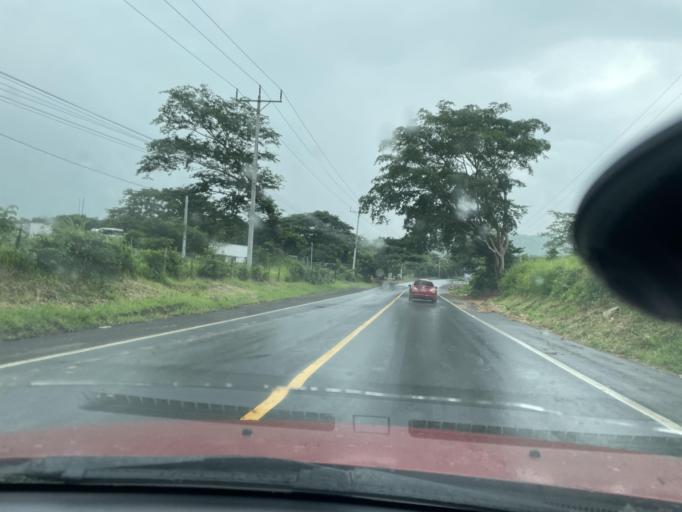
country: SV
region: San Miguel
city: San Miguel
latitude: 13.5419
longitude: -88.1262
